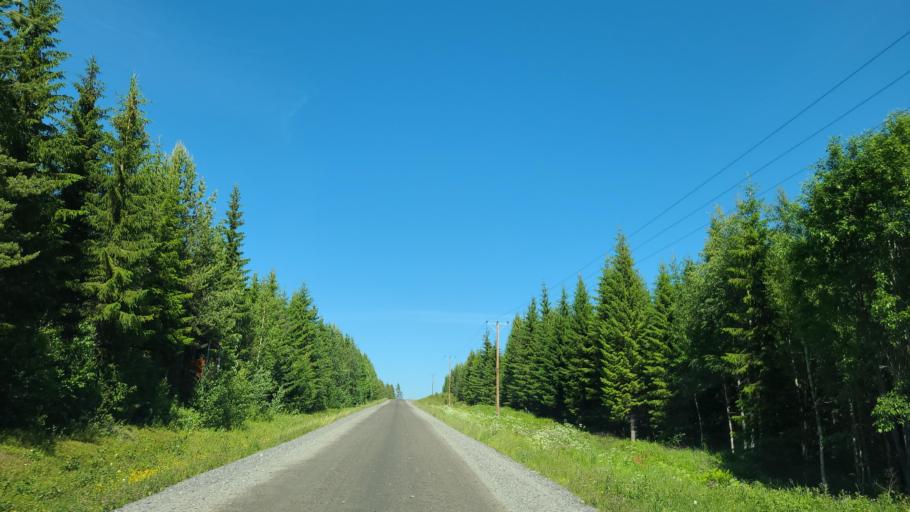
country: SE
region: Vaesterbotten
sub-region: Bjurholms Kommun
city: Bjurholm
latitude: 63.6413
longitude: 19.2105
